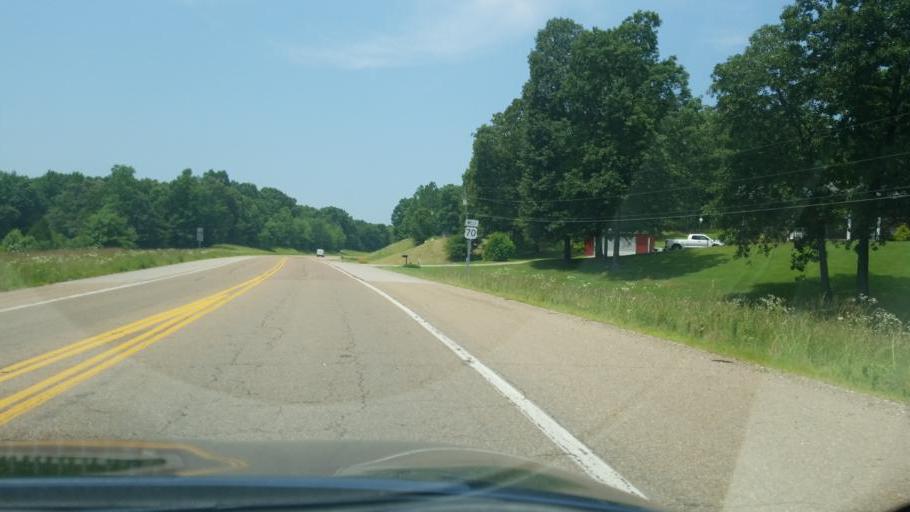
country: US
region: Tennessee
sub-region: Benton County
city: Camden
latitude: 36.0283
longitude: -88.0721
